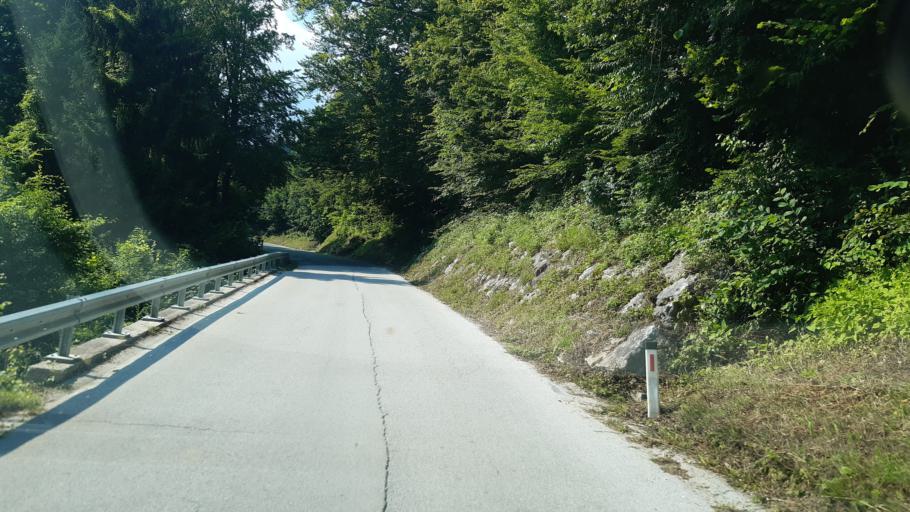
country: SI
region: Trzic
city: Bistrica pri Trzicu
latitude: 46.3600
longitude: 14.2454
